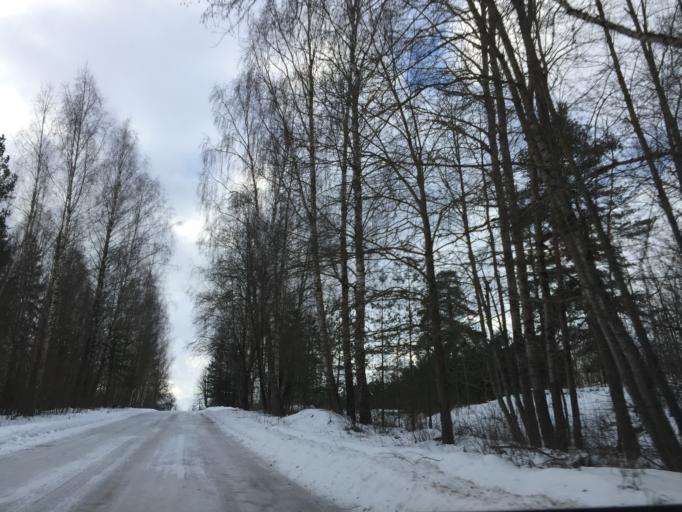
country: LV
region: Lielvarde
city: Lielvarde
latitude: 56.5749
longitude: 24.7360
